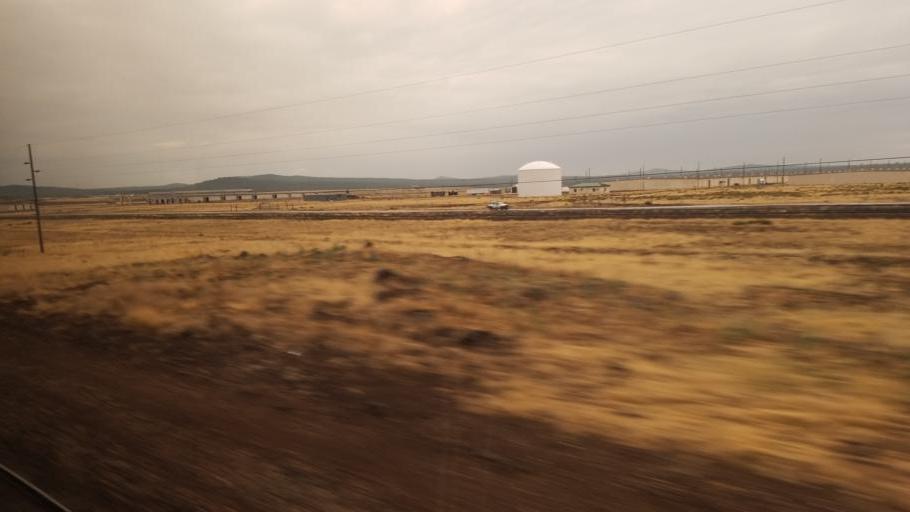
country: US
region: Arizona
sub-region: Coconino County
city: Parks
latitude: 35.2379
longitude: -111.8413
